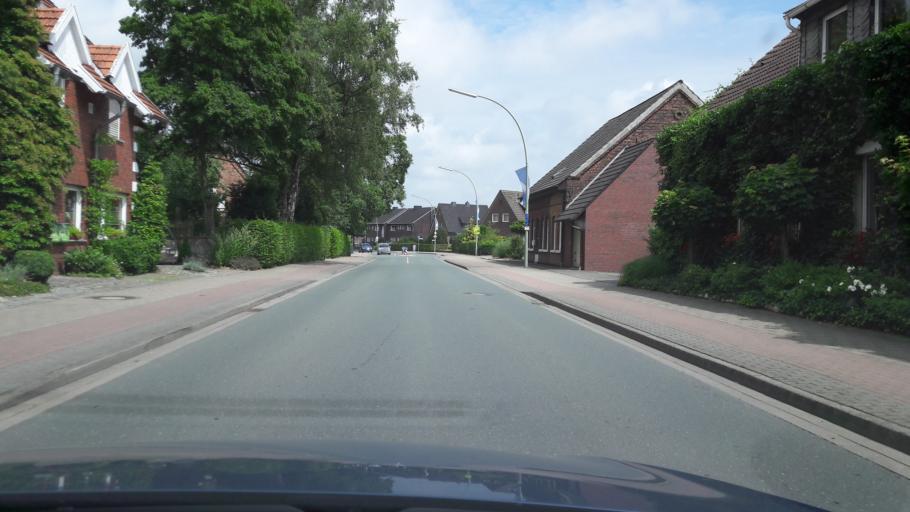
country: DE
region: North Rhine-Westphalia
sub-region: Regierungsbezirk Munster
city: Everswinkel
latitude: 51.9284
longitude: 7.8503
